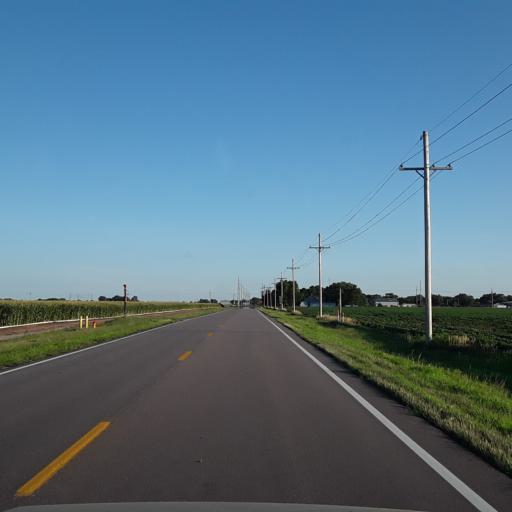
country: US
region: Nebraska
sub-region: Hall County
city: Grand Island
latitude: 40.9499
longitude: -98.3206
